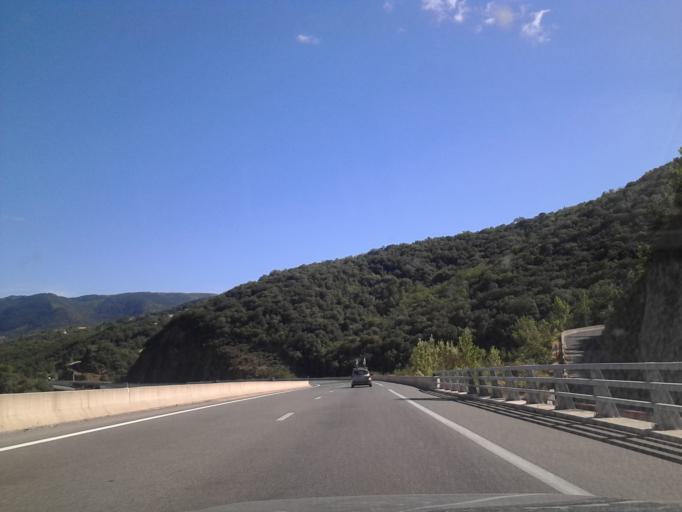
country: FR
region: Languedoc-Roussillon
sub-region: Departement de l'Herault
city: Lodeve
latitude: 43.7380
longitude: 3.3292
